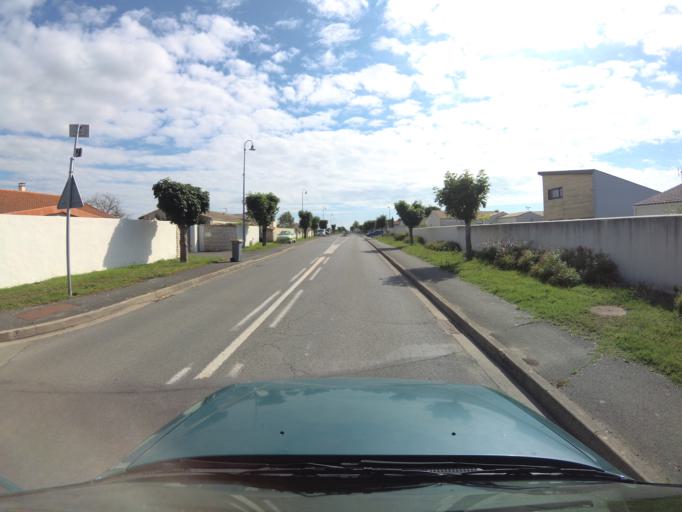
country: FR
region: Poitou-Charentes
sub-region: Departement de la Charente-Maritime
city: Andilly
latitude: 46.2380
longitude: -1.0701
